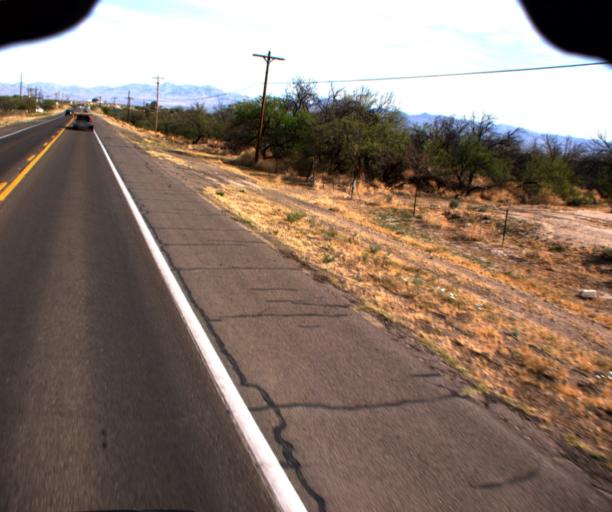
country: US
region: Arizona
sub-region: Graham County
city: Cactus Flat
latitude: 32.7704
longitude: -109.7163
